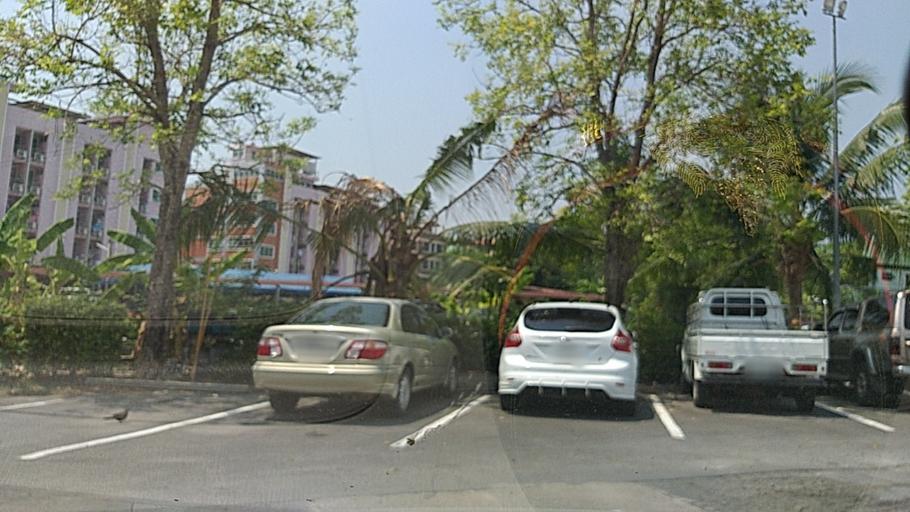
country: TH
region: Bangkok
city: Lak Si
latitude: 13.8725
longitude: 100.5921
